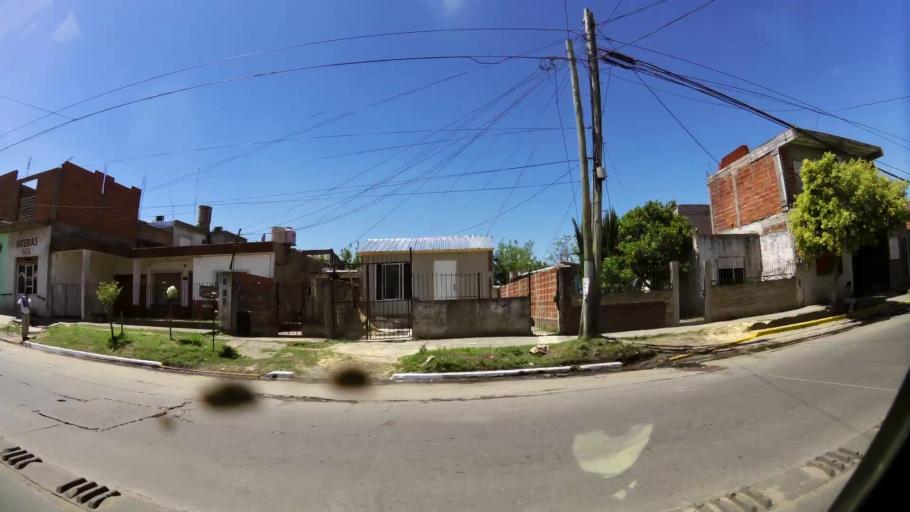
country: AR
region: Buenos Aires
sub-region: Partido de Quilmes
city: Quilmes
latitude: -34.7241
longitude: -58.3131
